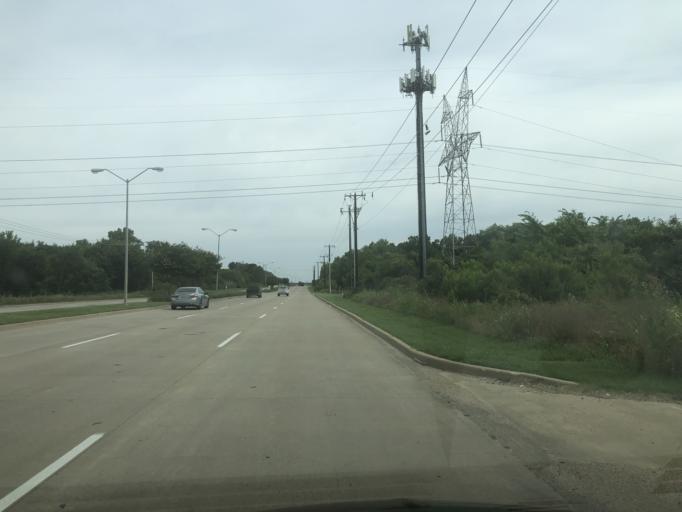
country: US
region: Texas
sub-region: Dallas County
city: Grand Prairie
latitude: 32.7838
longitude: -96.9946
